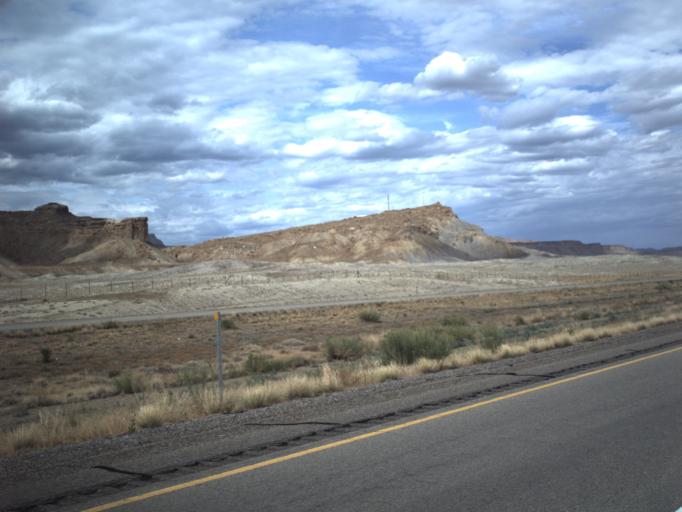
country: US
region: Utah
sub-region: Grand County
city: Moab
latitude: 38.9295
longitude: -109.8795
